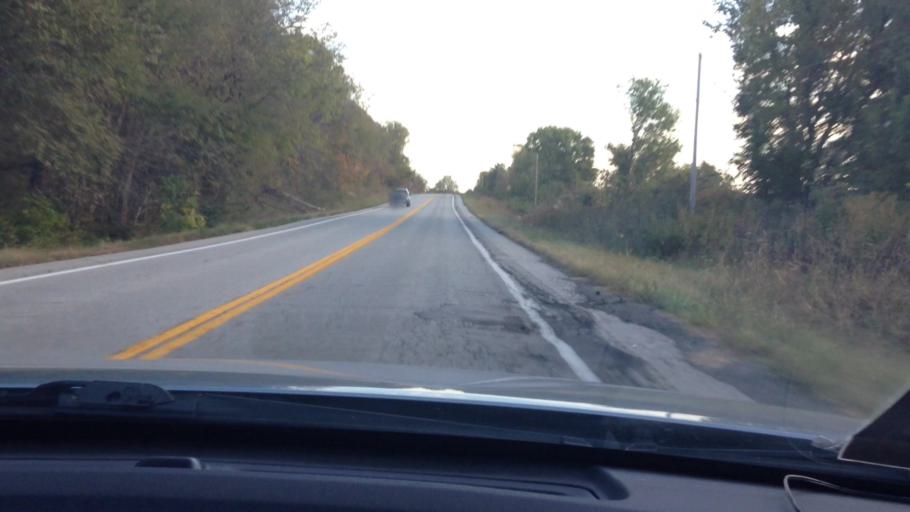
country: US
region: Kansas
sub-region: Leavenworth County
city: Lansing
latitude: 39.2437
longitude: -94.8033
